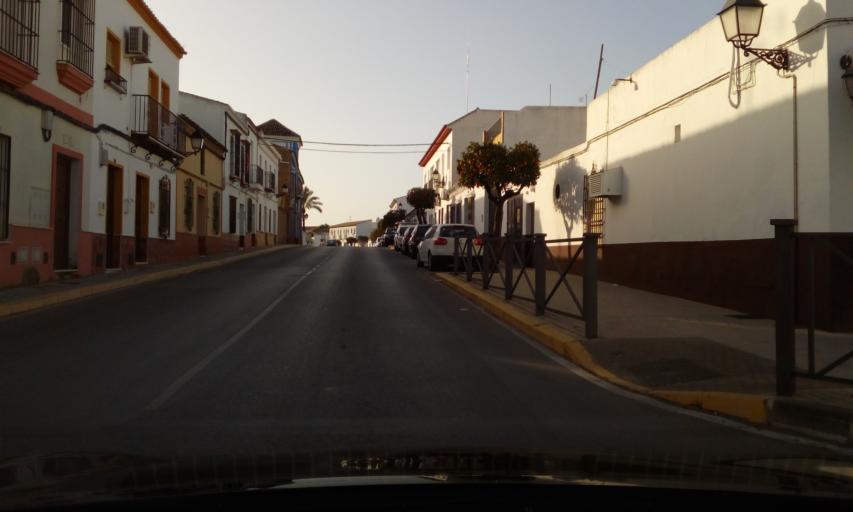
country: ES
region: Andalusia
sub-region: Provincia de Sevilla
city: Olivares
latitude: 37.4157
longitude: -6.1577
